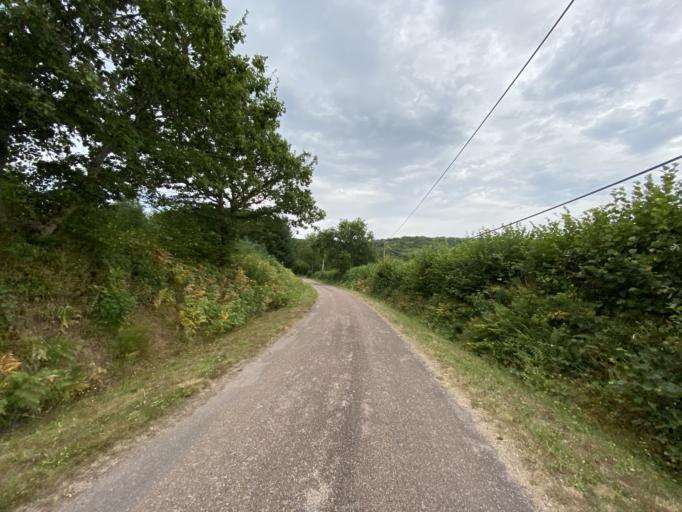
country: FR
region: Bourgogne
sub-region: Departement de la Cote-d'Or
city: Saulieu
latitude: 47.2672
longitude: 4.1487
